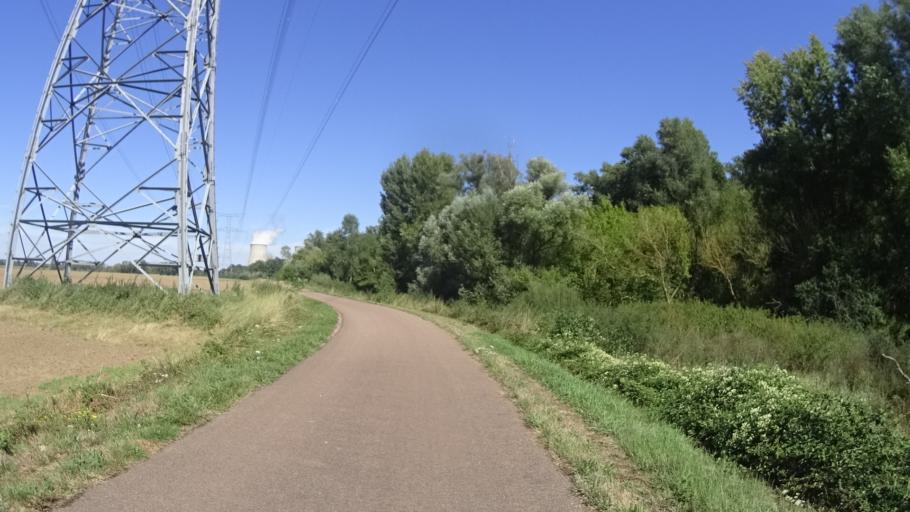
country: FR
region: Centre
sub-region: Departement du Cher
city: Lere
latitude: 47.4912
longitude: 2.8926
